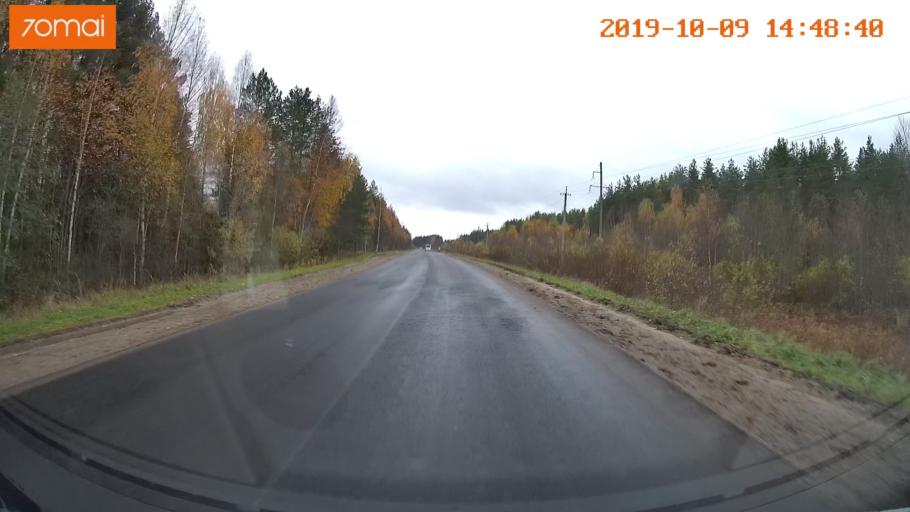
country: RU
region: Kostroma
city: Chistyye Bory
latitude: 58.4026
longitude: 41.5764
